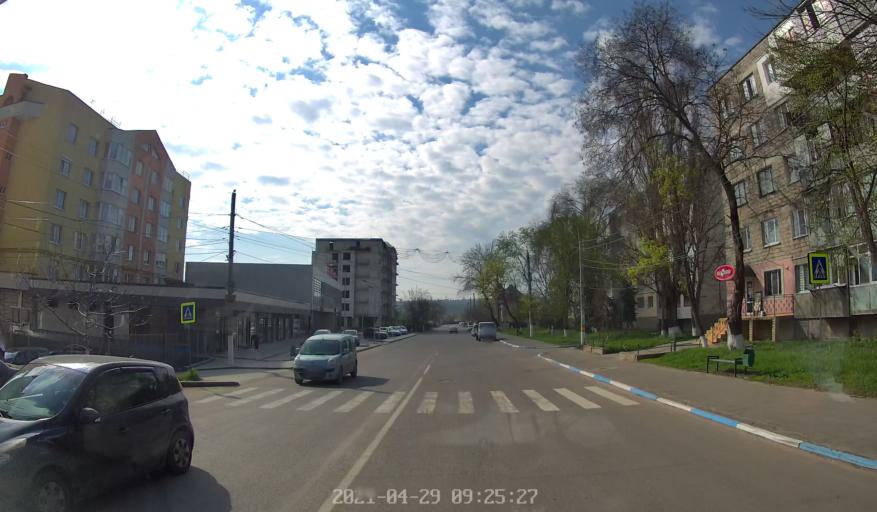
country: MD
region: Chisinau
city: Cricova
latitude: 47.1393
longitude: 28.8658
